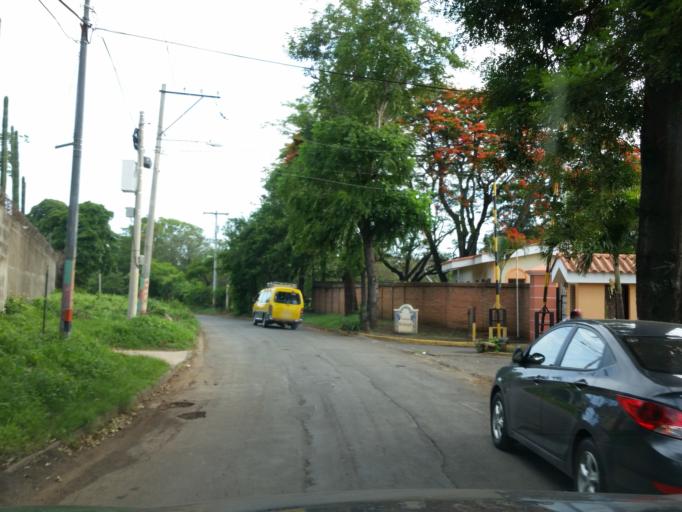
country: NI
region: Masaya
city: Ticuantepe
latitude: 12.0810
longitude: -86.2170
